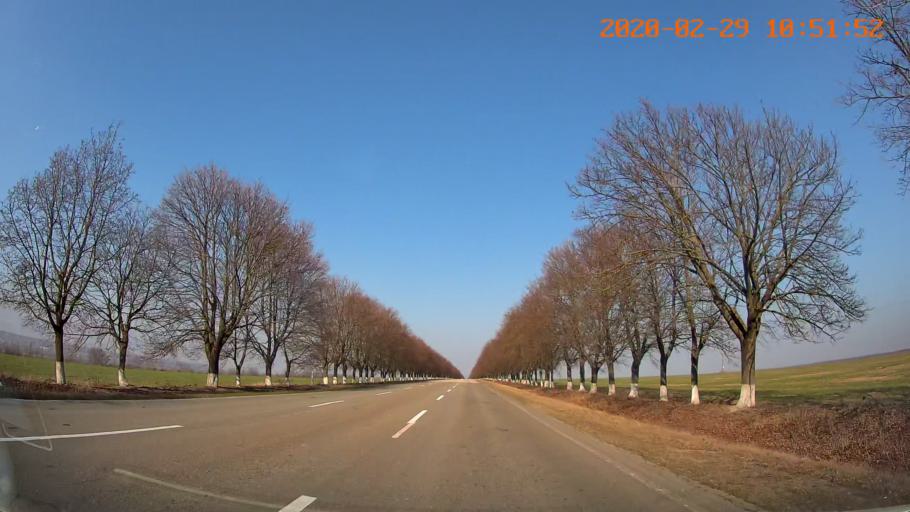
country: MD
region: Telenesti
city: Grigoriopol
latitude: 47.0982
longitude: 29.3582
